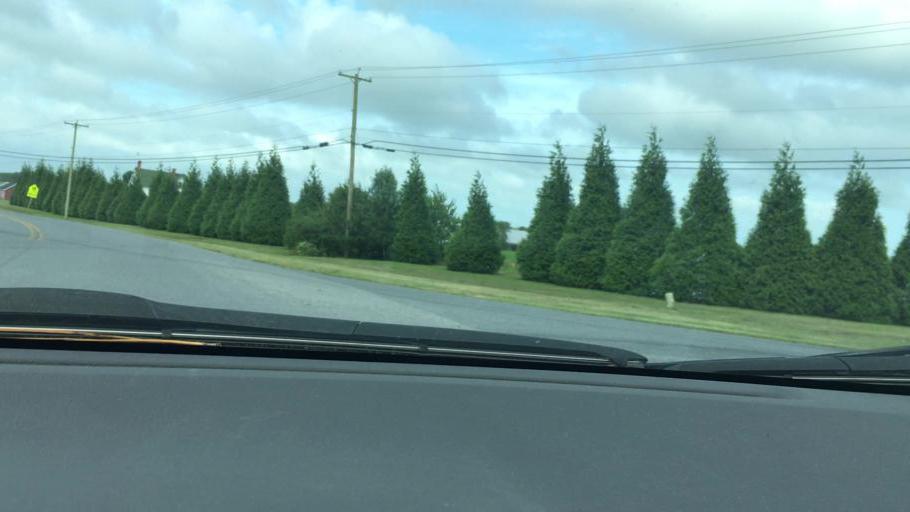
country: US
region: Maryland
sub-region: Worcester County
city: Pocomoke City
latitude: 38.0578
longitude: -75.5535
